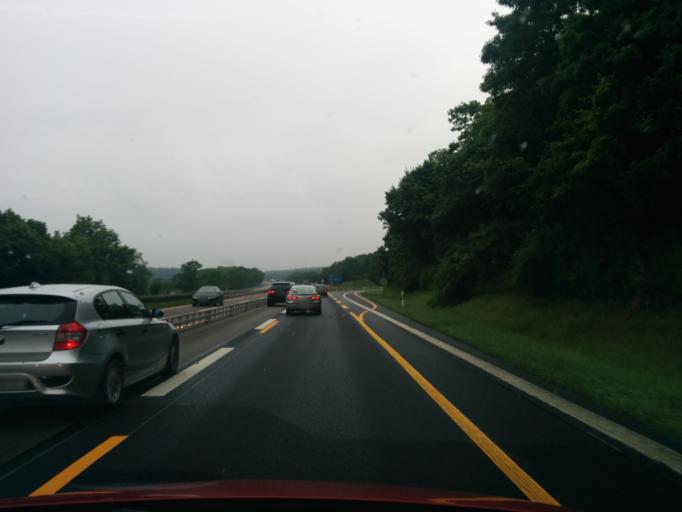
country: DE
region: Hesse
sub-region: Regierungsbezirk Kassel
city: Petersberg
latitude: 50.5801
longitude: 9.7120
